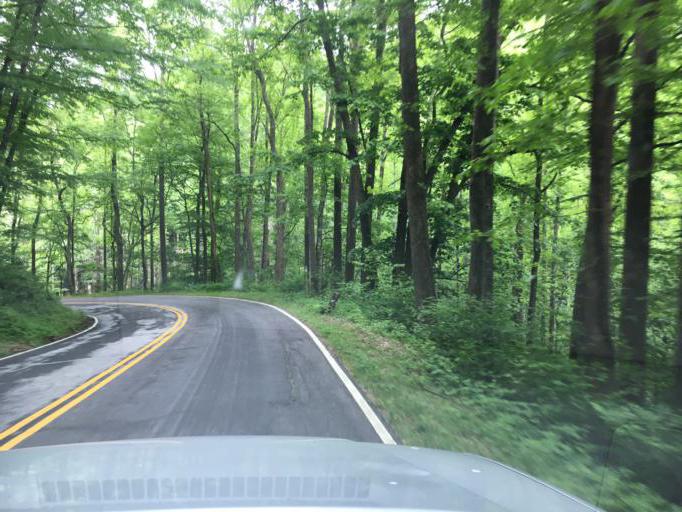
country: US
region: North Carolina
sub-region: Henderson County
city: Flat Rock
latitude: 35.1872
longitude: -82.4167
